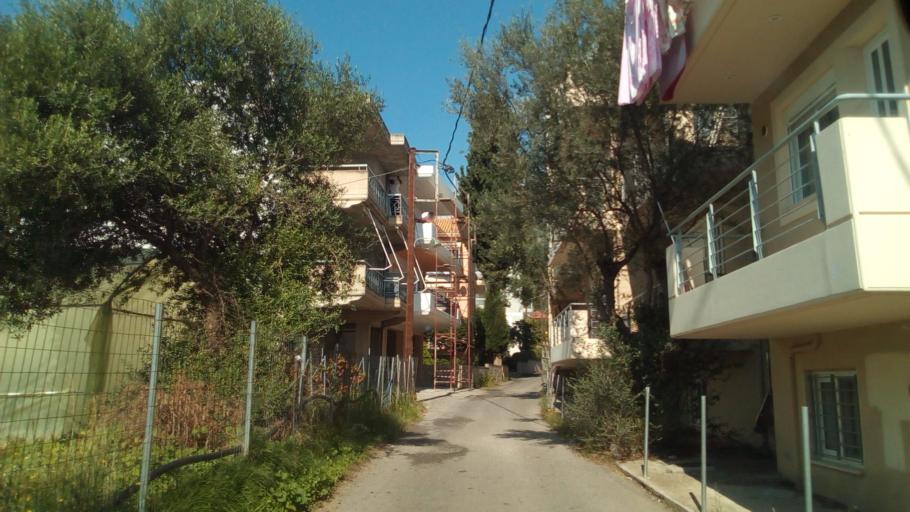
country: GR
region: West Greece
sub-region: Nomos Aitolias kai Akarnanias
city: Nafpaktos
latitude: 38.3911
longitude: 21.8183
